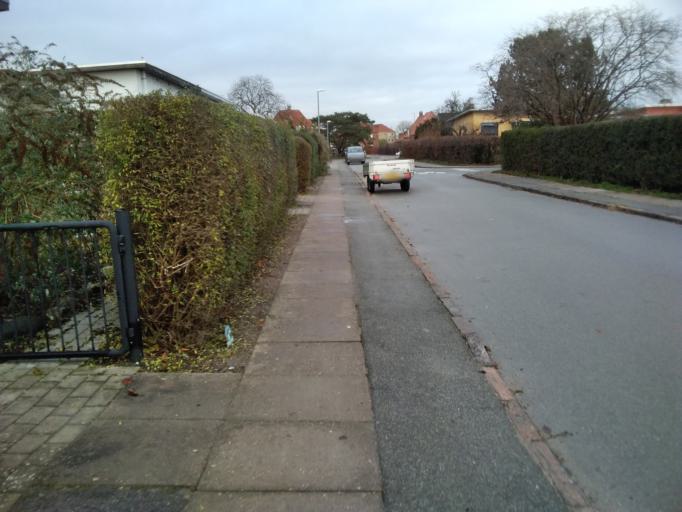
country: DK
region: Capital Region
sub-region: Tarnby Kommune
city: Tarnby
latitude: 55.6433
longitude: 12.6269
